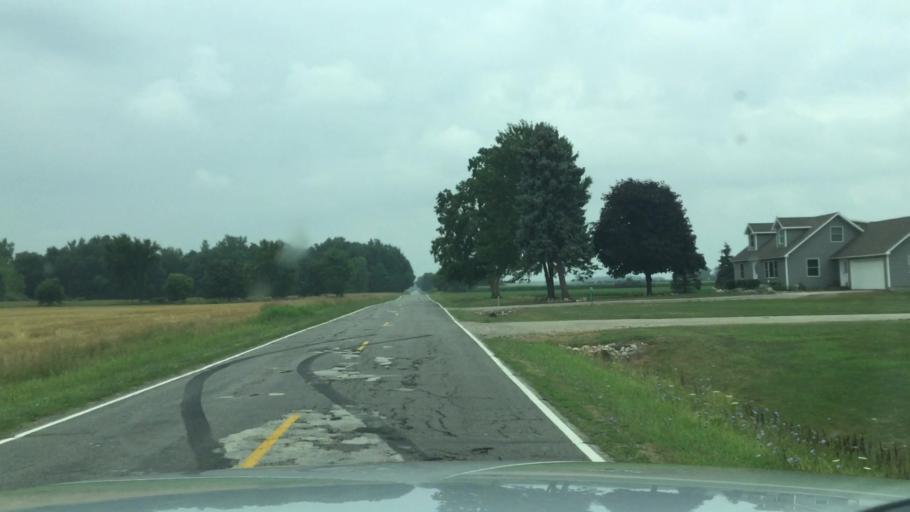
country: US
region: Michigan
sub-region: Shiawassee County
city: New Haven
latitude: 43.0810
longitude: -84.2262
